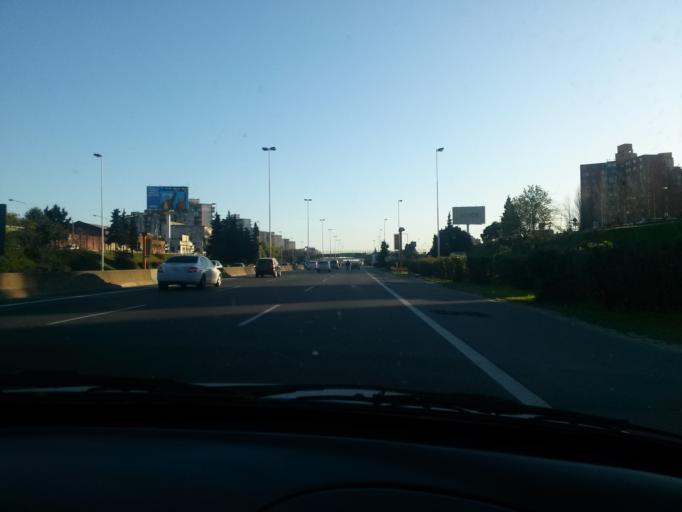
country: AR
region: Buenos Aires F.D.
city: Villa Lugano
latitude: -34.6924
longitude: -58.4899
